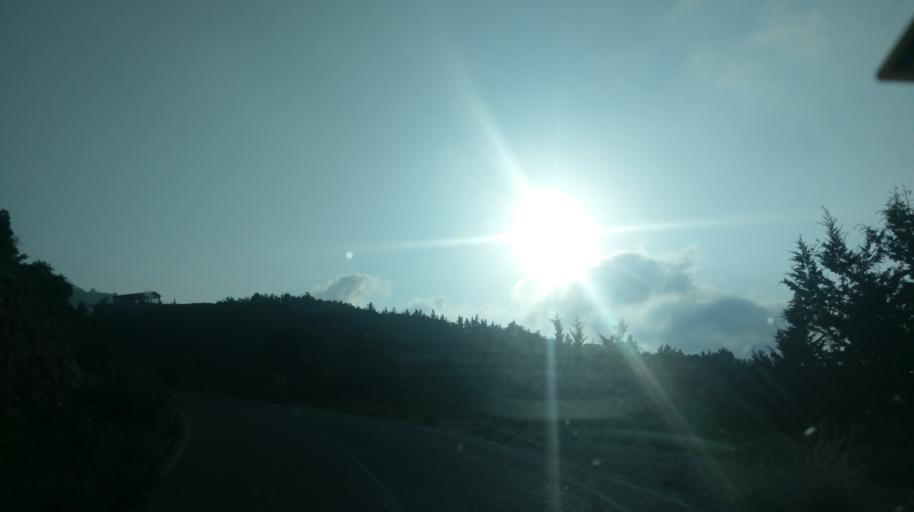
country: CY
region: Ammochostos
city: Trikomo
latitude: 35.4061
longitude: 33.9047
